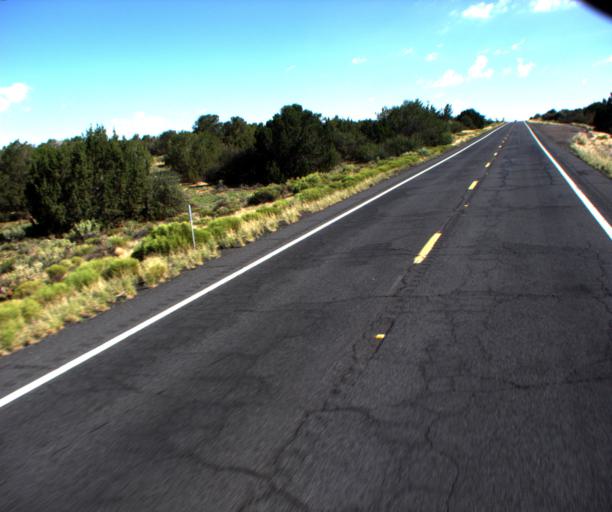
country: US
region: Arizona
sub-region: Coconino County
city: Williams
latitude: 35.5203
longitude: -112.1695
